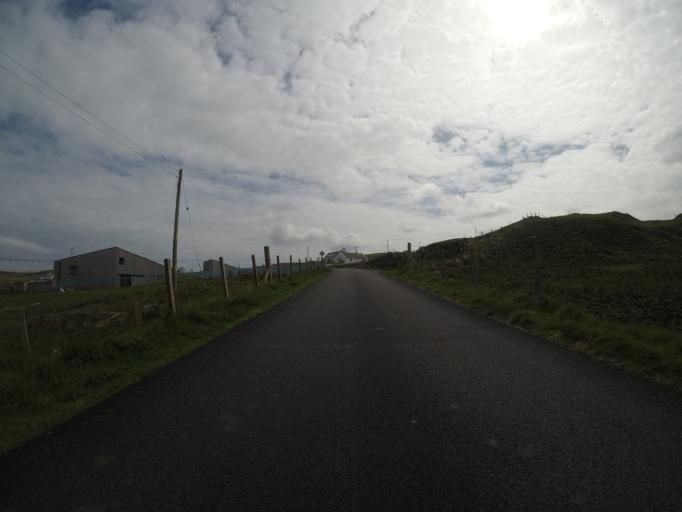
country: GB
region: Scotland
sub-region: Highland
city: Portree
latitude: 57.6834
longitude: -6.3001
